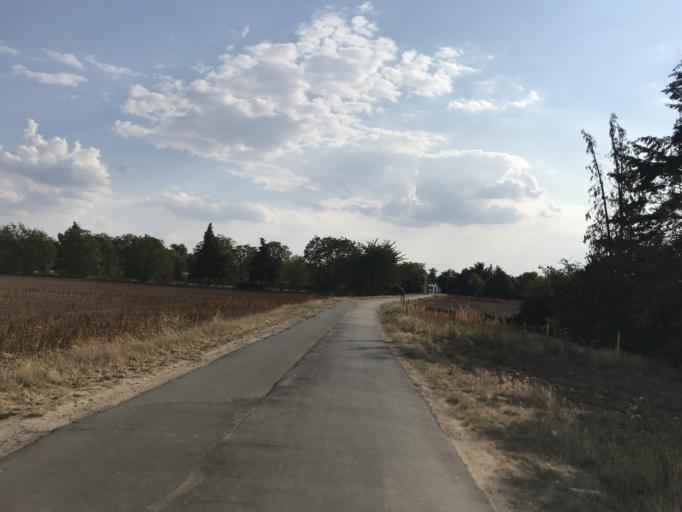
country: DE
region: Rheinland-Pfalz
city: Mainz
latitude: 50.0194
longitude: 8.2946
